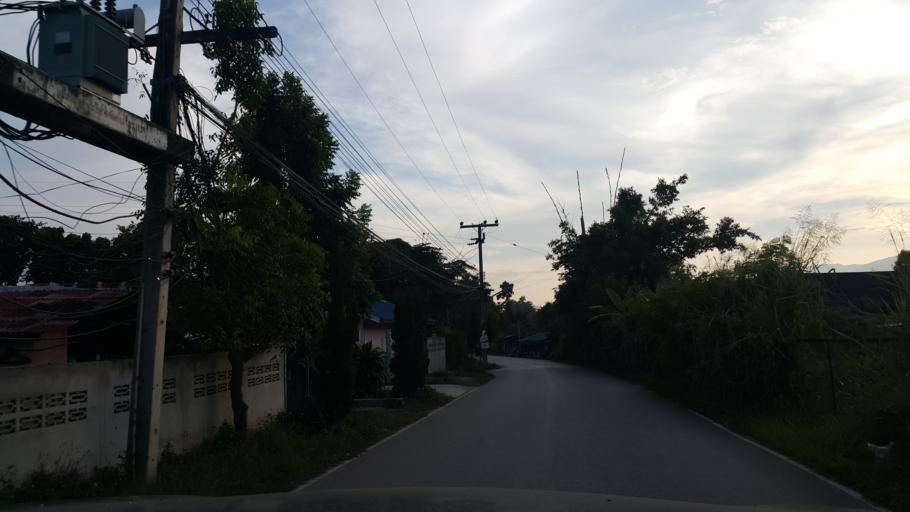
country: TH
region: Chiang Mai
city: San Sai
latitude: 18.9051
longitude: 99.0428
